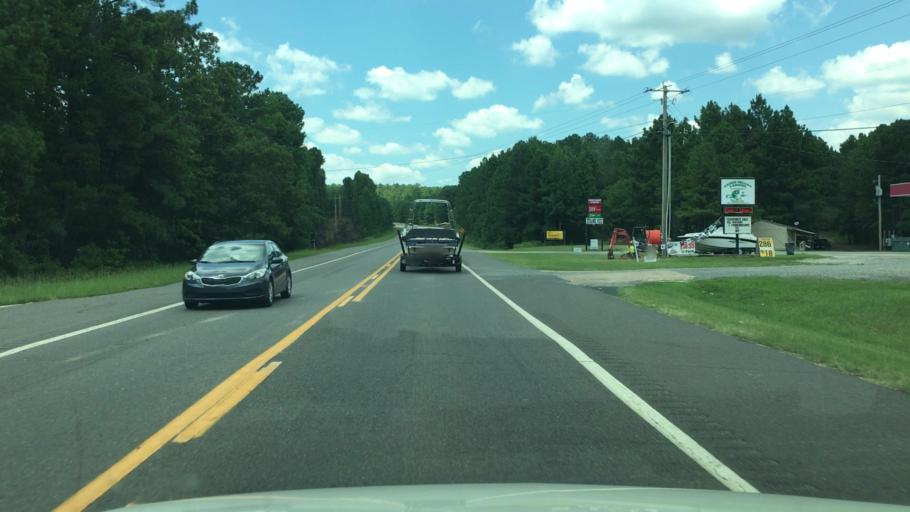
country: US
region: Arkansas
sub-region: Clark County
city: Arkadelphia
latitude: 34.2053
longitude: -93.0788
